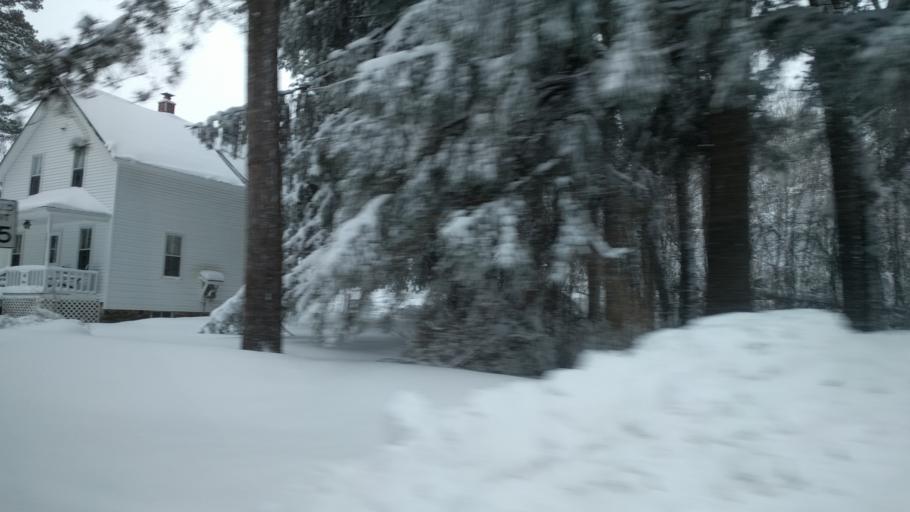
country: US
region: Wisconsin
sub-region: Iron County
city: Hurley
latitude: 46.4281
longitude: -90.2457
